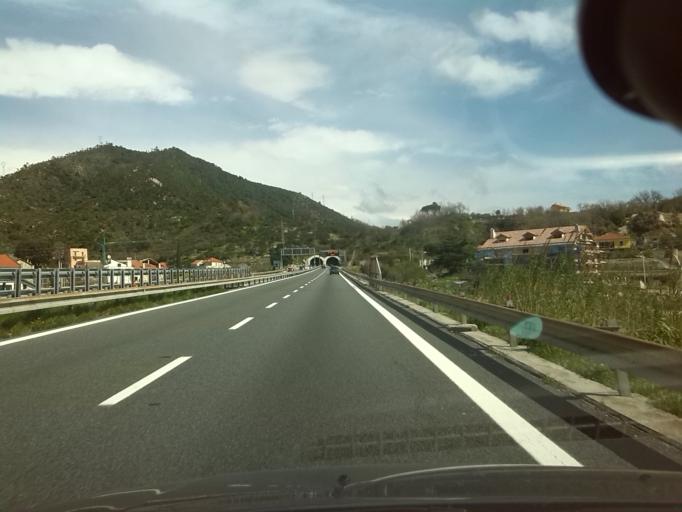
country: IT
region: Liguria
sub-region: Provincia di Savona
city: Loano
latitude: 44.1386
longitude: 8.2433
